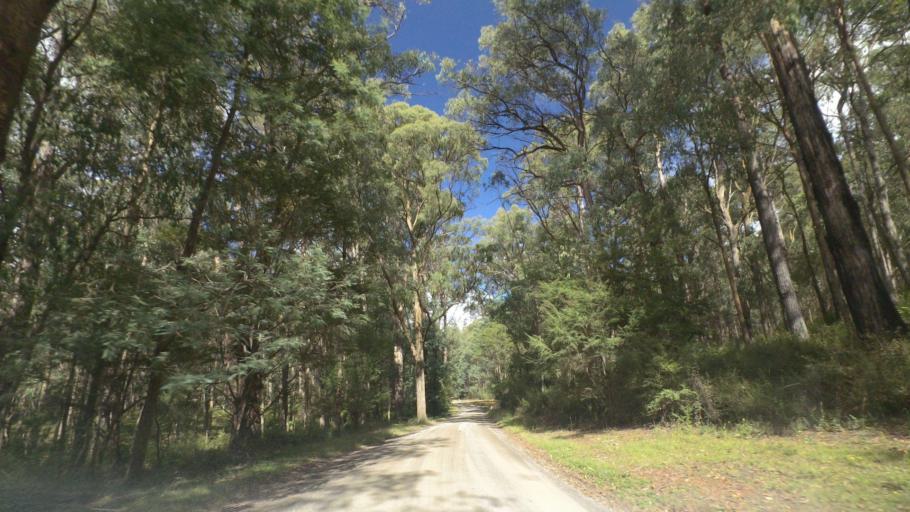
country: AU
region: Victoria
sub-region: Cardinia
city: Gembrook
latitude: -37.8854
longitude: 145.6206
